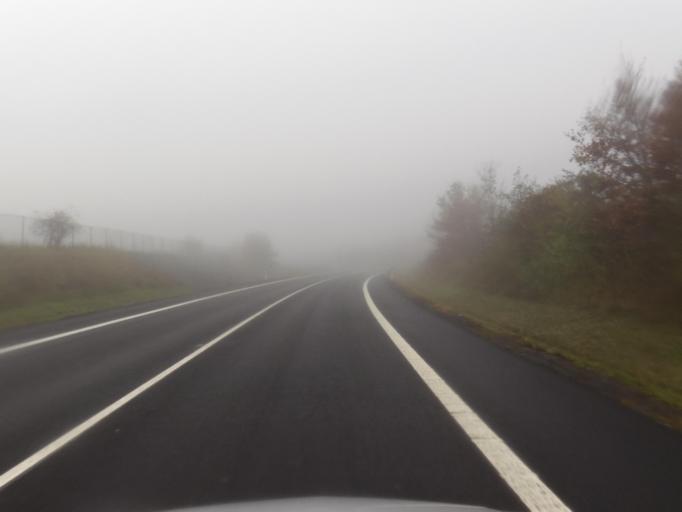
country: CZ
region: Ustecky
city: Libouchec
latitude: 50.7236
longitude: 14.0041
